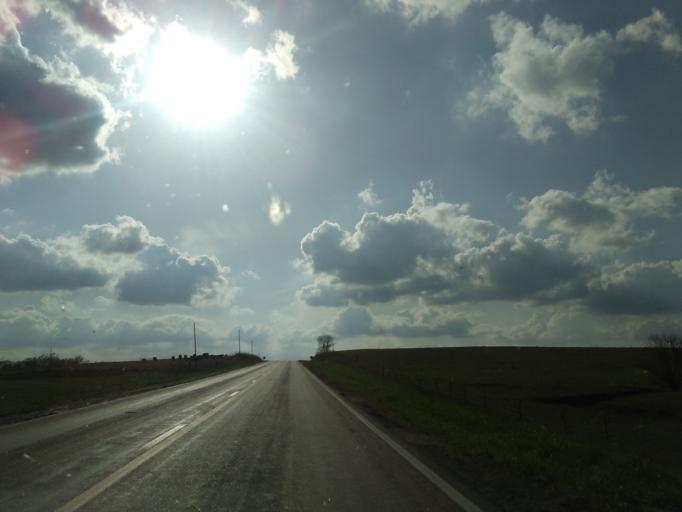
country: US
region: Nebraska
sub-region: Webster County
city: Red Cloud
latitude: 40.0889
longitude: -98.5715
